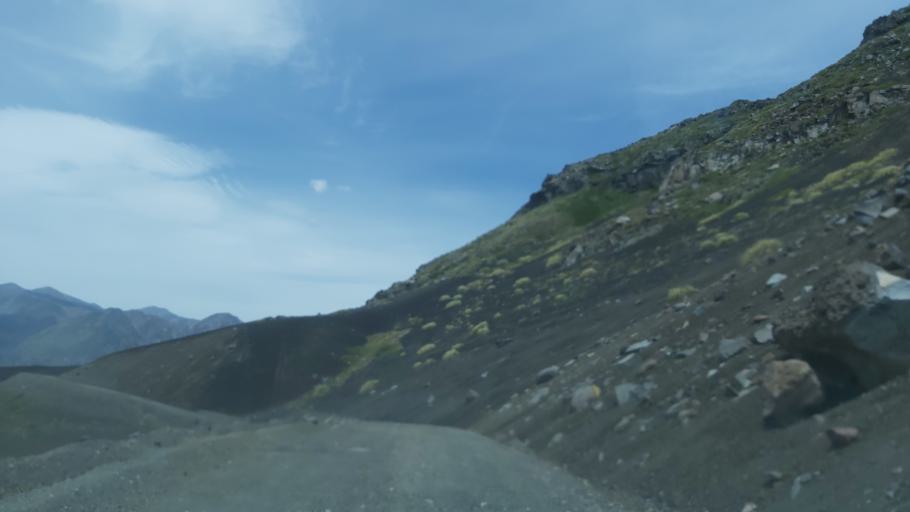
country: AR
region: Neuquen
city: Andacollo
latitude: -37.4087
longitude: -71.2972
